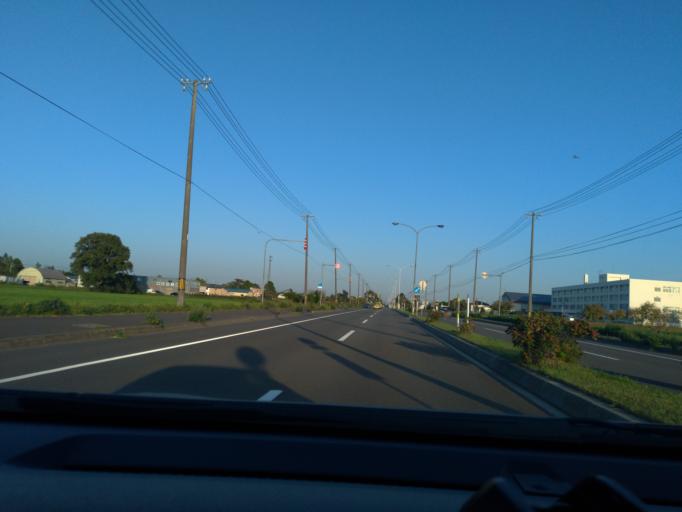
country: JP
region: Hokkaido
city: Ishikari
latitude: 43.1608
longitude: 141.3672
